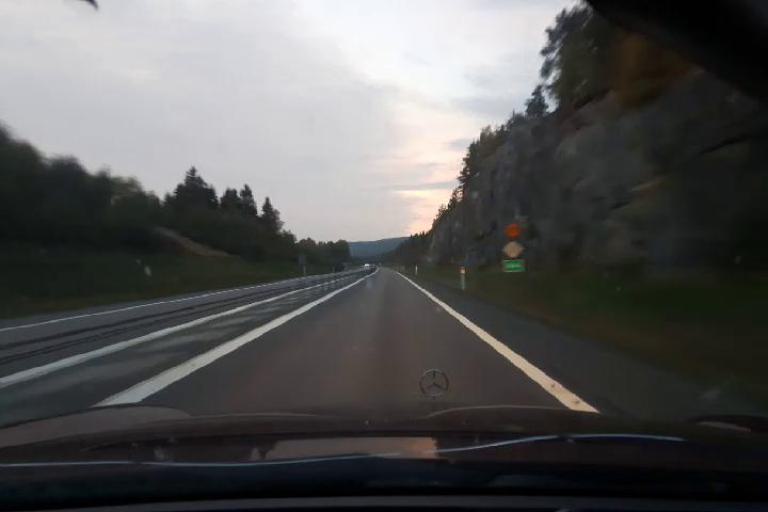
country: SE
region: Vaesternorrland
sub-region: Kramfors Kommun
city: Nordingra
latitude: 62.9318
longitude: 18.0960
